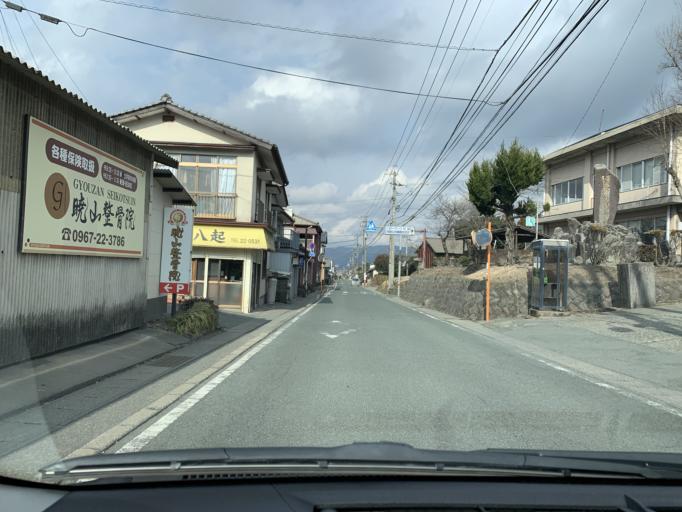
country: JP
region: Kumamoto
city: Aso
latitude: 32.9395
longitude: 131.1151
